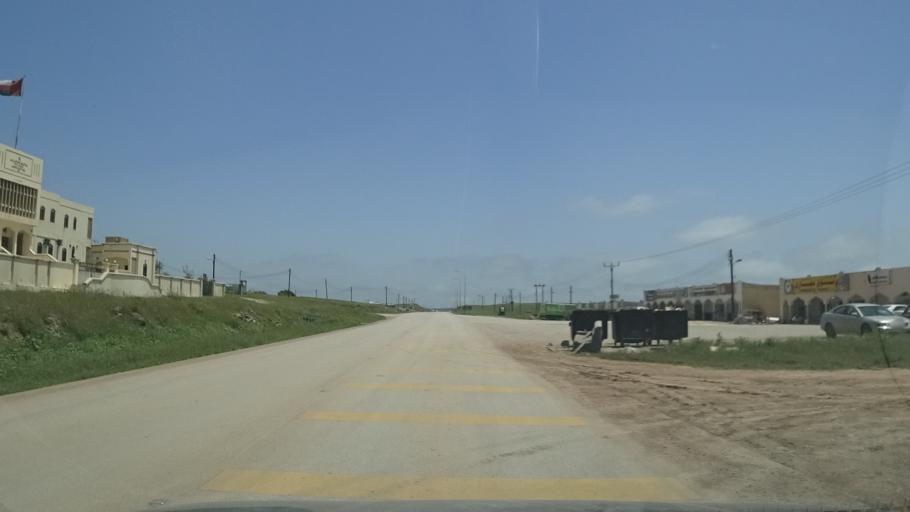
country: OM
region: Zufar
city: Salalah
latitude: 17.2421
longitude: 54.2833
